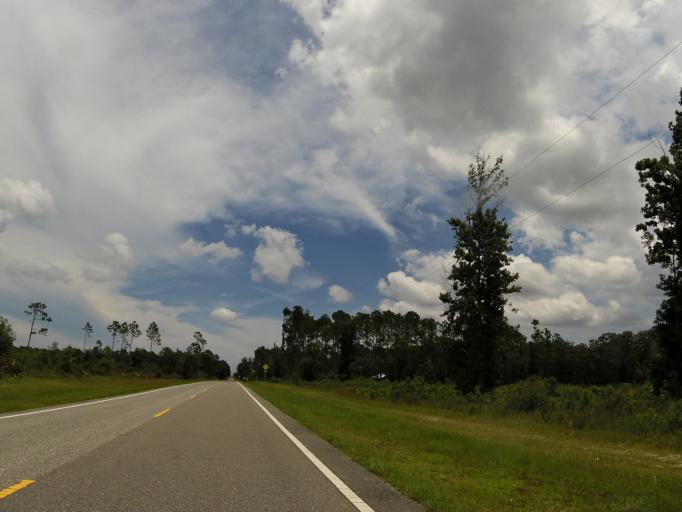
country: US
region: Florida
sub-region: Flagler County
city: Palm Coast
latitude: 29.6555
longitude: -81.3346
